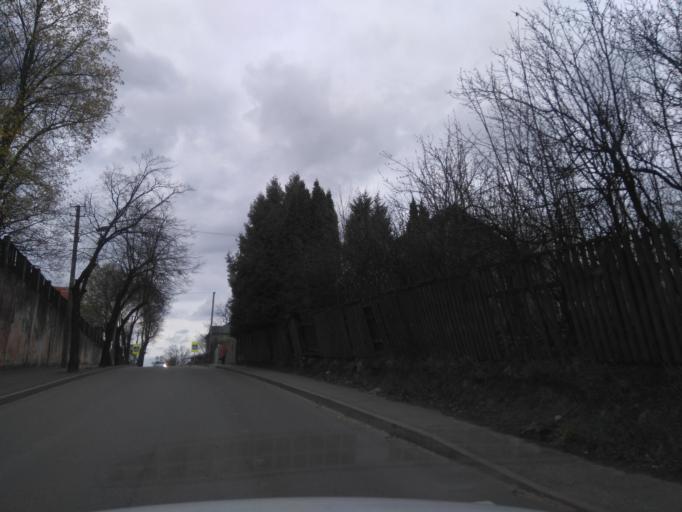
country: LT
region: Kauno apskritis
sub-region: Kaunas
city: Aleksotas
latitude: 54.8766
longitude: 23.9427
